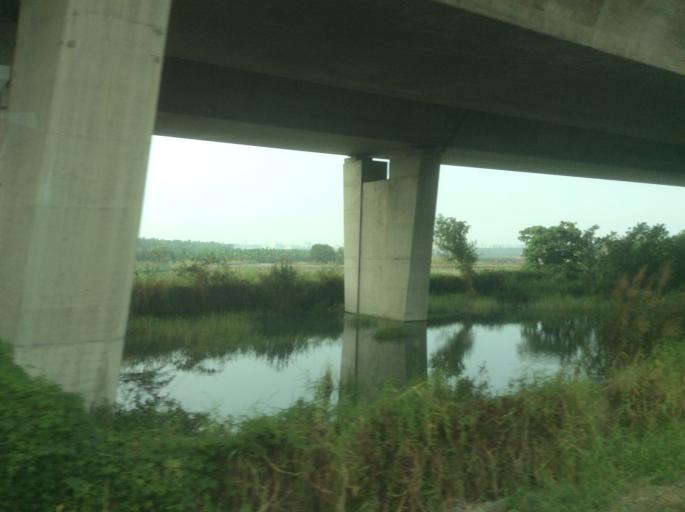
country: TW
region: Taiwan
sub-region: Yunlin
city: Douliu
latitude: 23.7439
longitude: 120.5920
